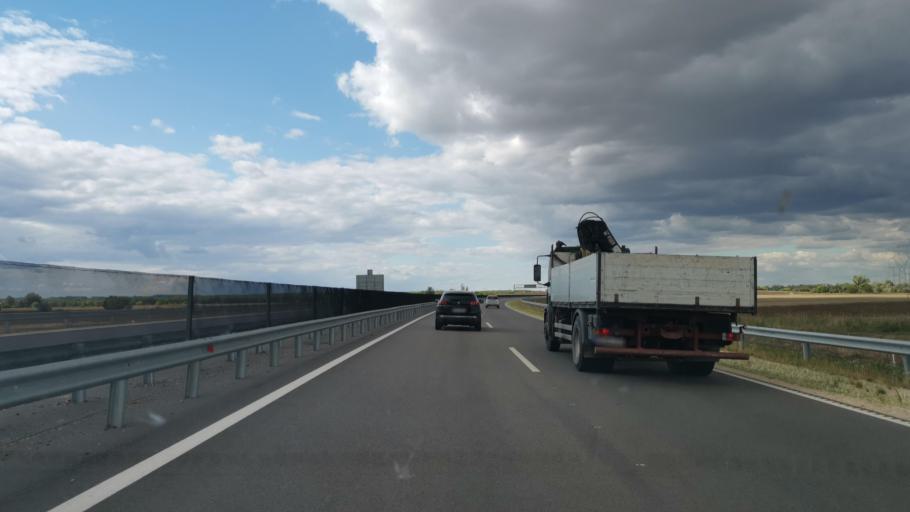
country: HU
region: Jasz-Nagykun-Szolnok
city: Tiszapuspoki
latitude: 47.1890
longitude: 20.3420
